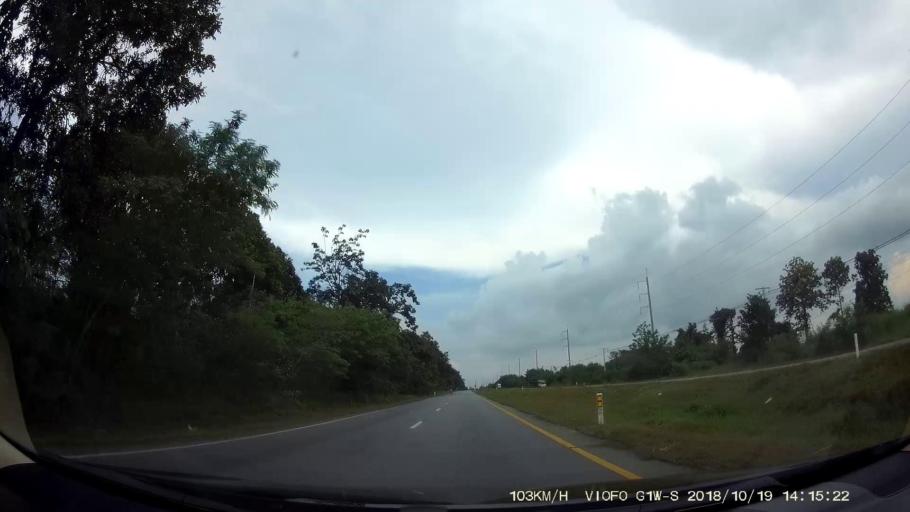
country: TH
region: Chaiyaphum
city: Khon Sawan
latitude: 15.9821
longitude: 102.1991
